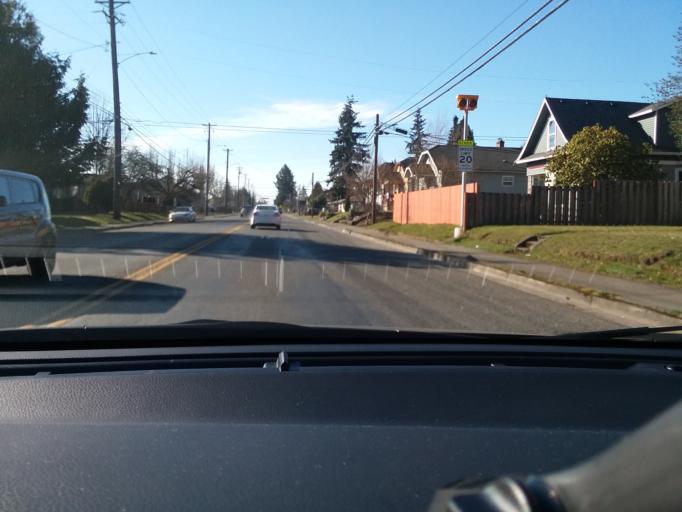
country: US
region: Washington
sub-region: Pierce County
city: Midland
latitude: 47.2108
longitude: -122.4209
